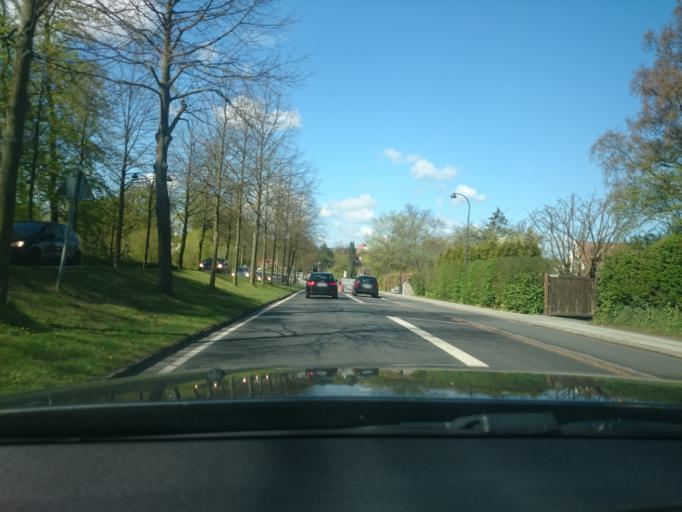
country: DK
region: Capital Region
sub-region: Lyngby-Tarbaek Kommune
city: Kongens Lyngby
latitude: 55.7614
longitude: 12.5472
